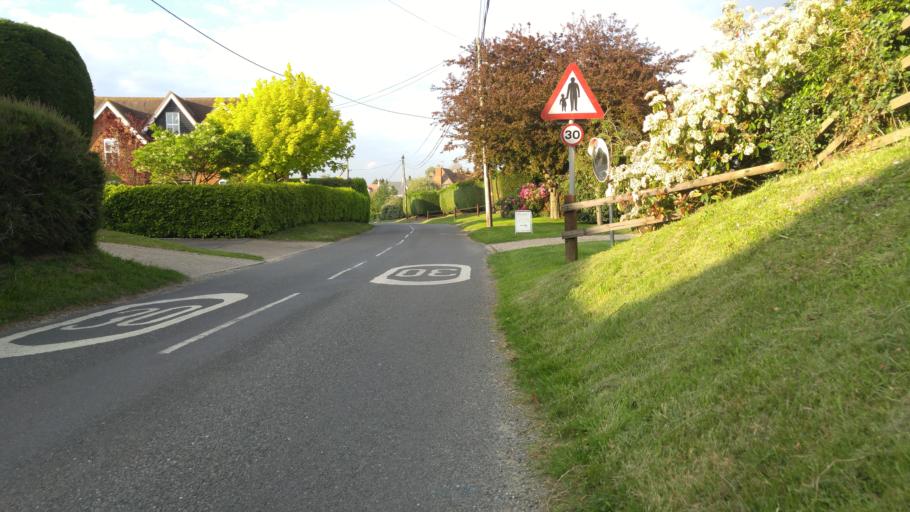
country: GB
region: England
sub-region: Essex
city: Tiptree
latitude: 51.8329
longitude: 0.7488
